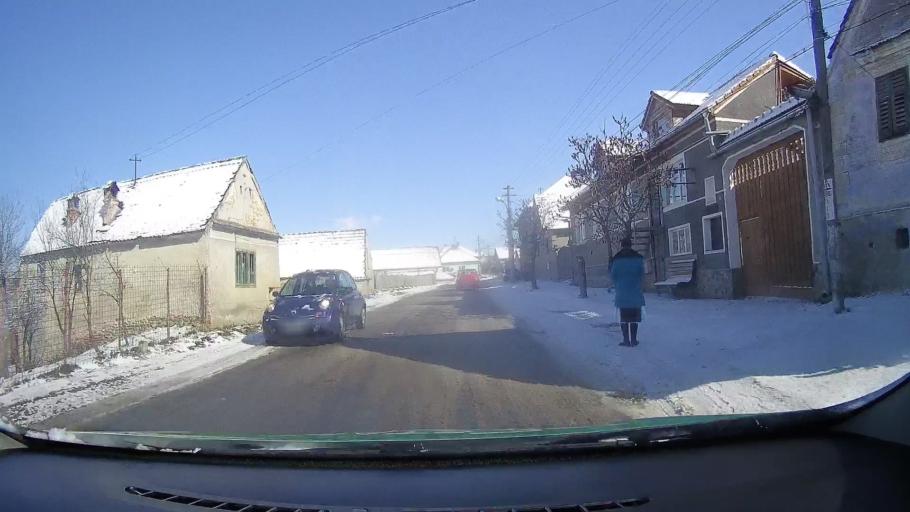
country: RO
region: Sibiu
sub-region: Comuna Avrig
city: Avrig
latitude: 45.7231
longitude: 24.3721
